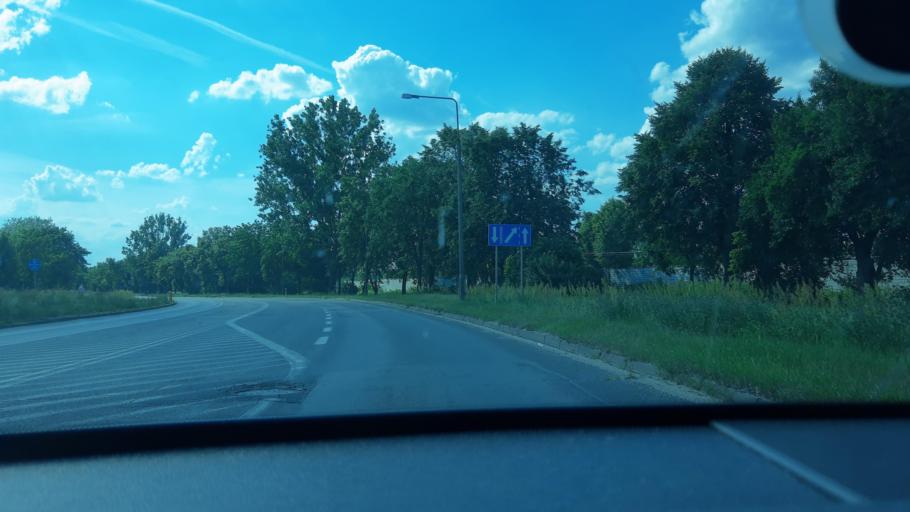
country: PL
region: Lodz Voivodeship
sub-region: Powiat zdunskowolski
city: Zdunska Wola
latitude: 51.6069
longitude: 18.9377
